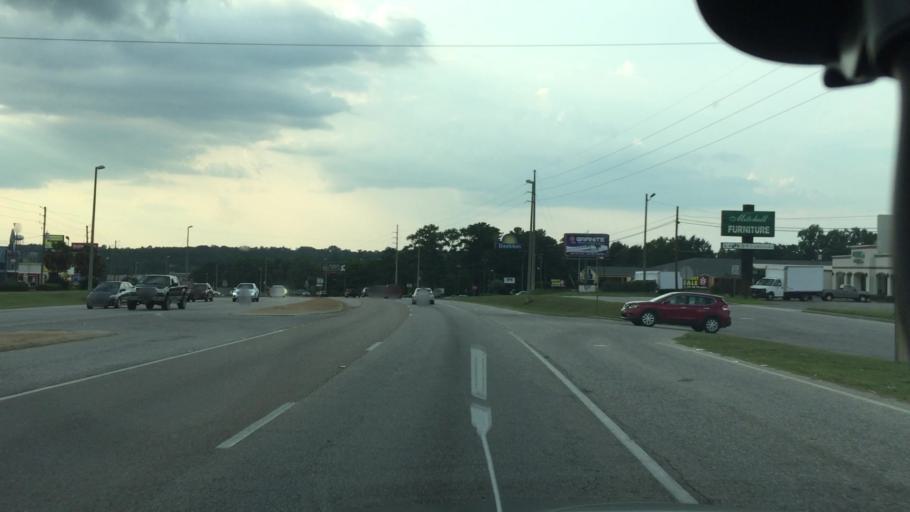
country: US
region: Alabama
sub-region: Coffee County
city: Enterprise
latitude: 31.3245
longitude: -85.8318
